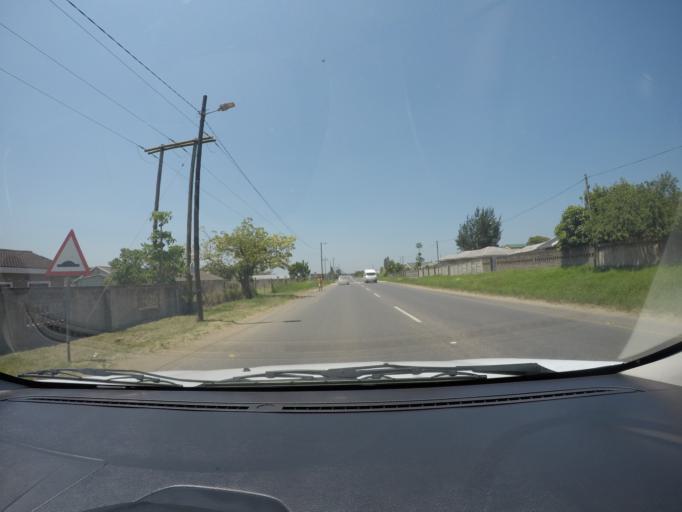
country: ZA
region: KwaZulu-Natal
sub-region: uThungulu District Municipality
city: eSikhawini
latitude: -28.8827
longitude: 31.8882
